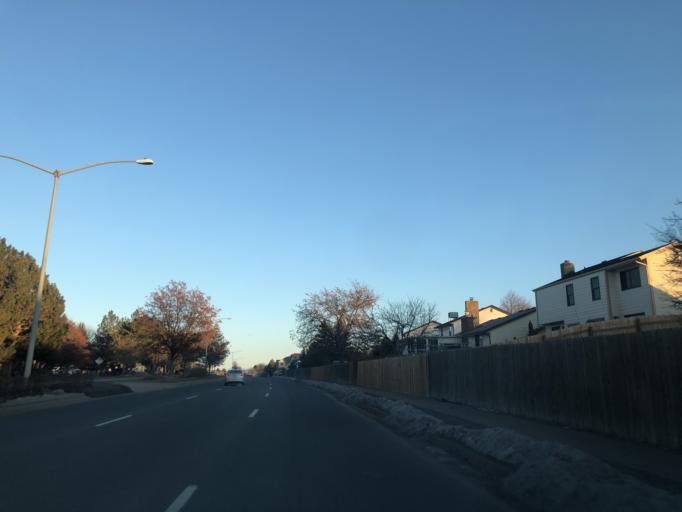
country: US
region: Colorado
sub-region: Adams County
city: Aurora
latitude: 39.7070
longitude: -104.8003
